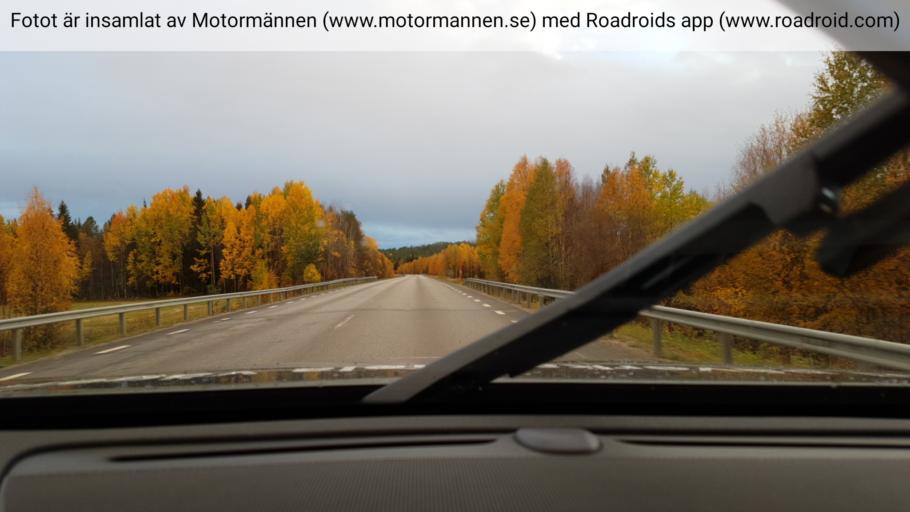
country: SE
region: Norrbotten
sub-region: Overkalix Kommun
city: OEverkalix
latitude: 66.3573
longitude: 22.8314
